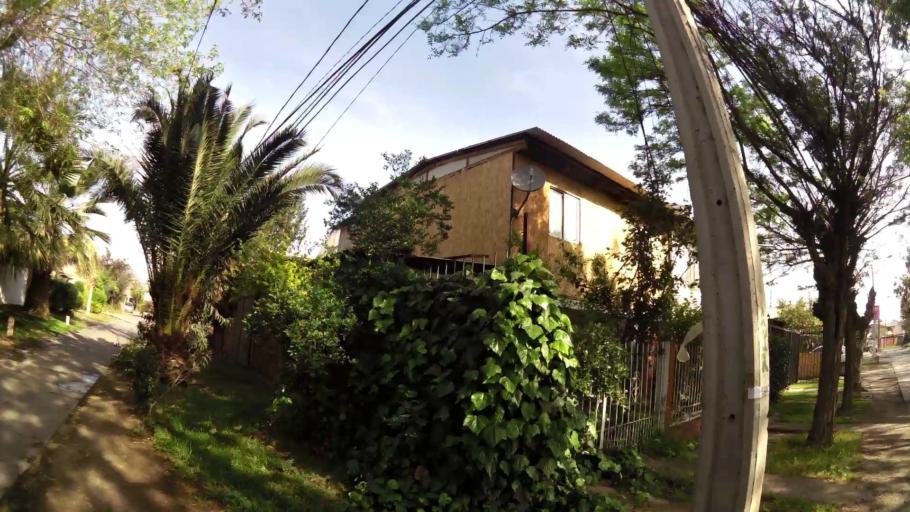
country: CL
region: Santiago Metropolitan
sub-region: Provincia de Santiago
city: Villa Presidente Frei, Nunoa, Santiago, Chile
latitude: -33.5184
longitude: -70.5869
